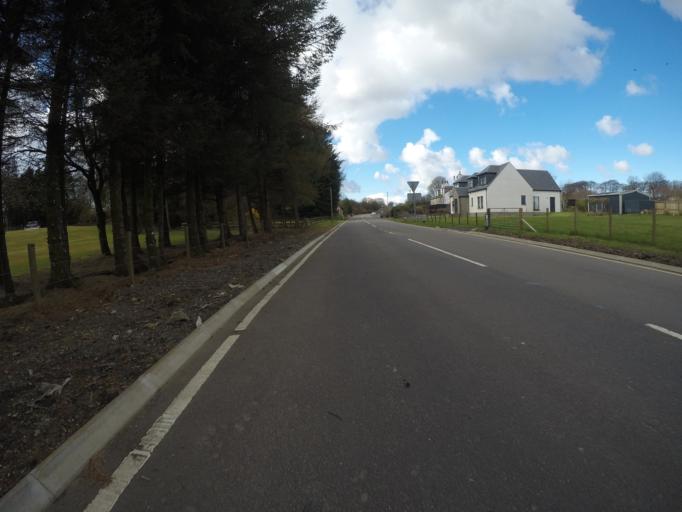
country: GB
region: Scotland
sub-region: North Ayrshire
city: Kilbirnie
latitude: 55.7263
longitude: -4.6653
